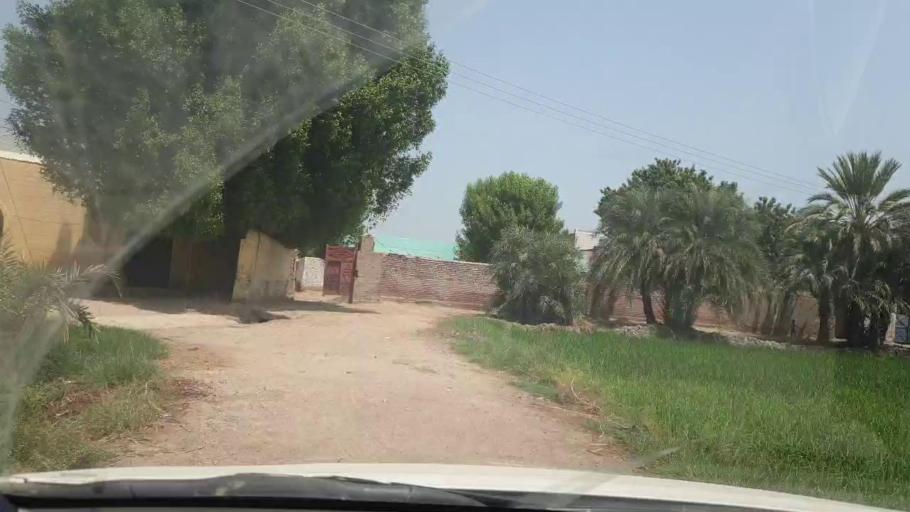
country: PK
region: Sindh
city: Shikarpur
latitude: 27.9362
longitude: 68.6697
